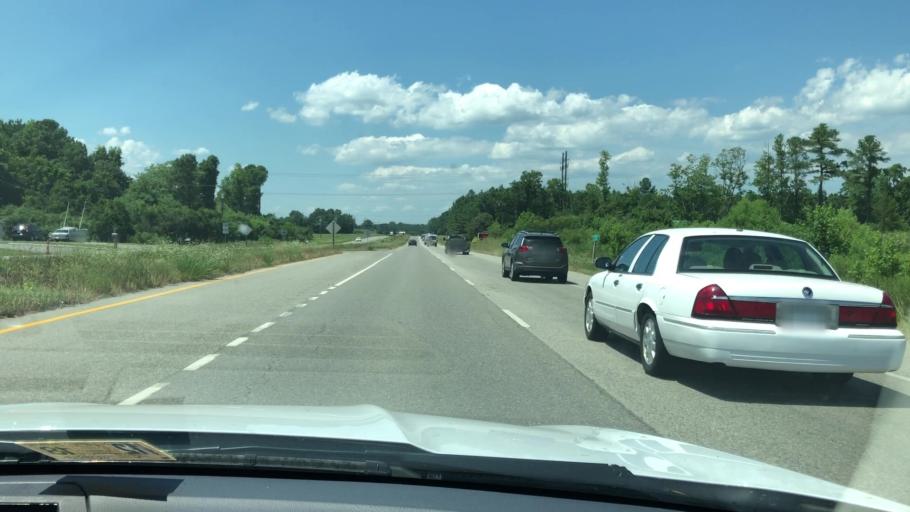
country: US
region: Virginia
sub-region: Middlesex County
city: Saluda
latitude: 37.5831
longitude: -76.4884
